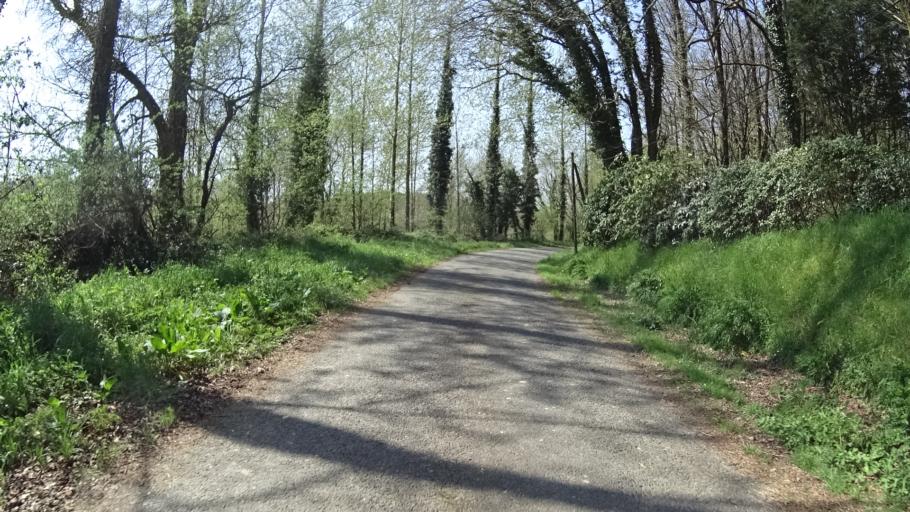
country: FR
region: Brittany
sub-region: Departement du Finistere
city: Sizun
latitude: 48.4132
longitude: -4.0881
